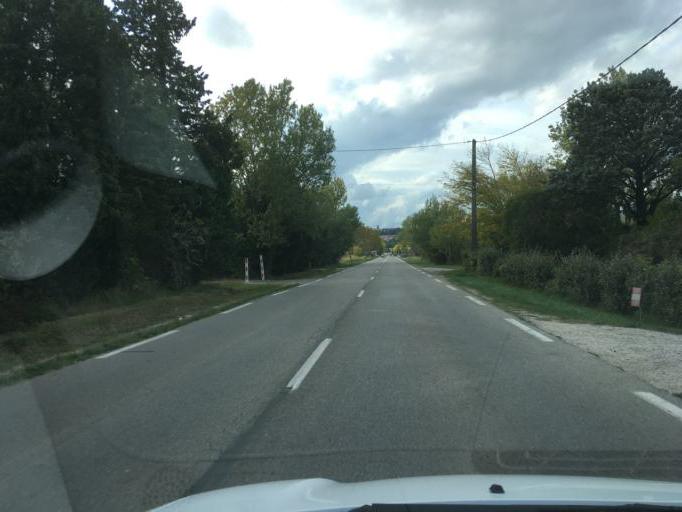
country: FR
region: Provence-Alpes-Cote d'Azur
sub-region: Departement du Vaucluse
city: Chateauneuf-de-Gadagne
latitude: 43.9244
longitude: 4.9644
